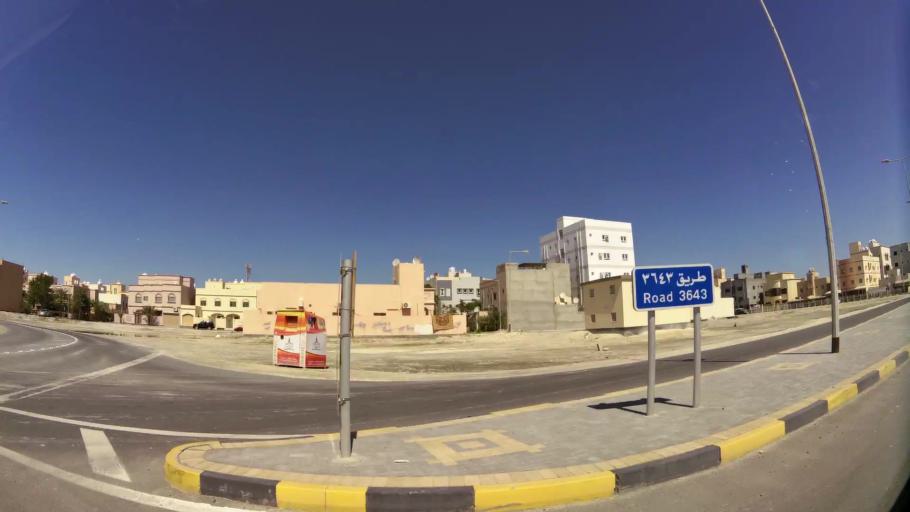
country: BH
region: Muharraq
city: Al Muharraq
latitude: 26.2768
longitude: 50.6400
